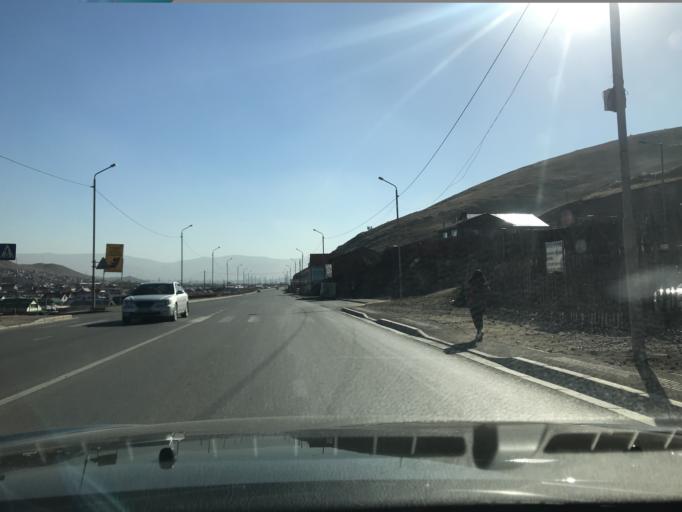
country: MN
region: Ulaanbaatar
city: Ulaanbaatar
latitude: 47.9894
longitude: 106.9251
